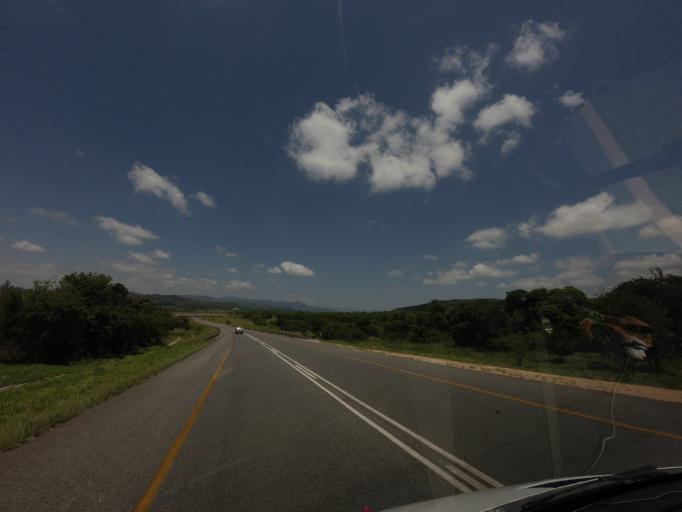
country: ZA
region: Mpumalanga
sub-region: Ehlanzeni District
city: Nelspruit
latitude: -25.4395
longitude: 30.9412
